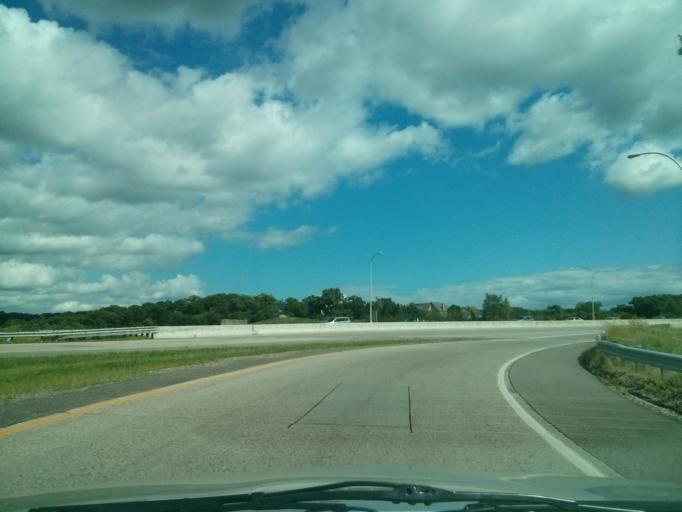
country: US
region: Minnesota
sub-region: Dakota County
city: Apple Valley
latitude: 44.7795
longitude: -93.2182
